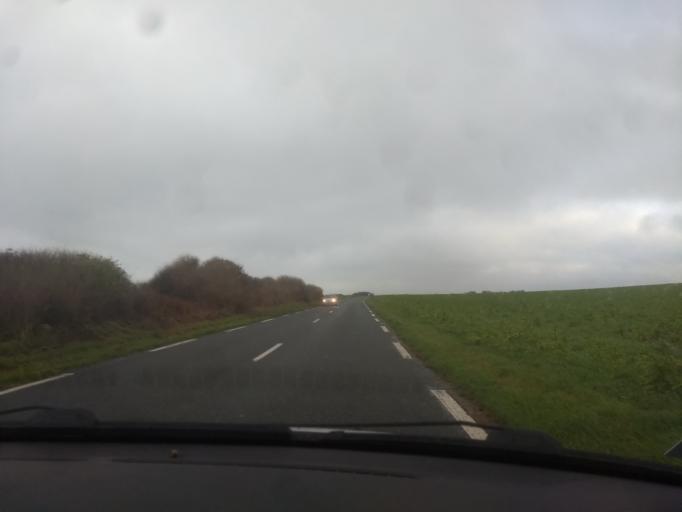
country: FR
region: Nord-Pas-de-Calais
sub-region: Departement du Pas-de-Calais
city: Sangatte
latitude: 50.9369
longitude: 1.7291
